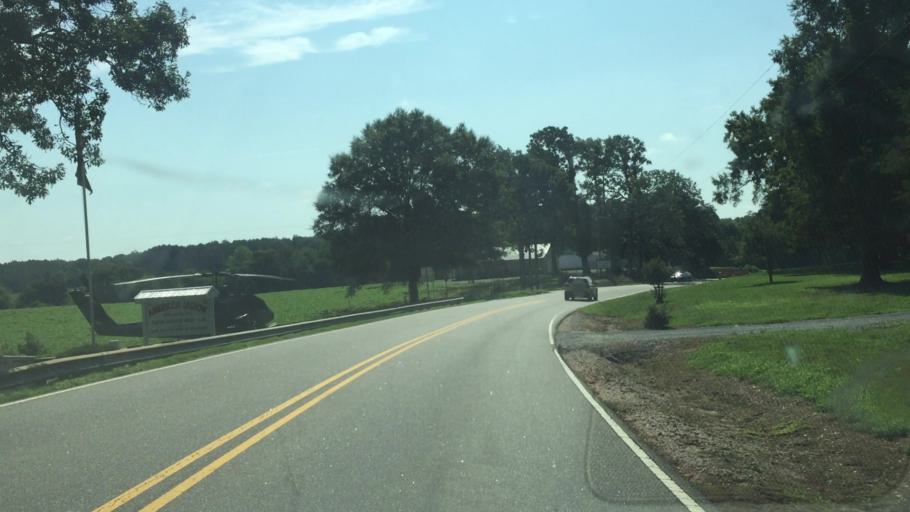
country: US
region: North Carolina
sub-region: Stanly County
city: Oakboro
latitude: 35.1350
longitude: -80.3754
